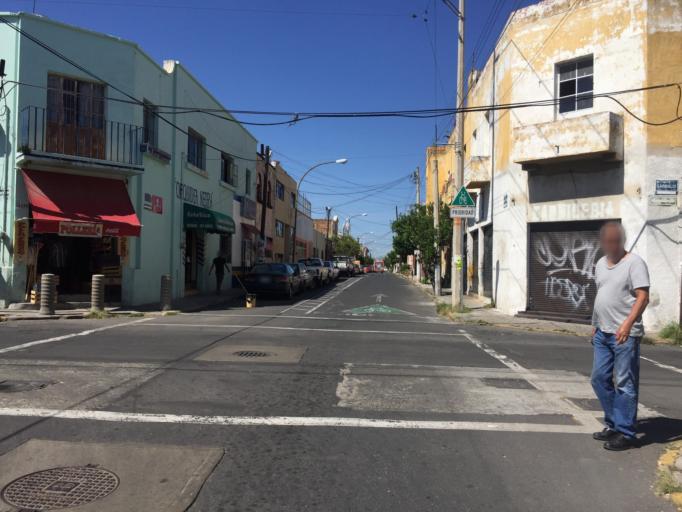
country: MX
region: Jalisco
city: Guadalajara
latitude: 20.6810
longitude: -103.3621
